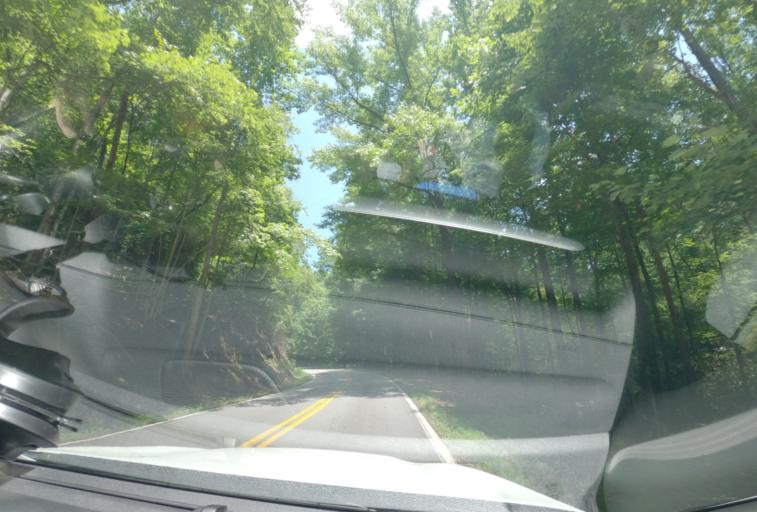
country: US
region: South Carolina
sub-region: Pickens County
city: Pickens
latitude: 35.0011
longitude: -82.8206
